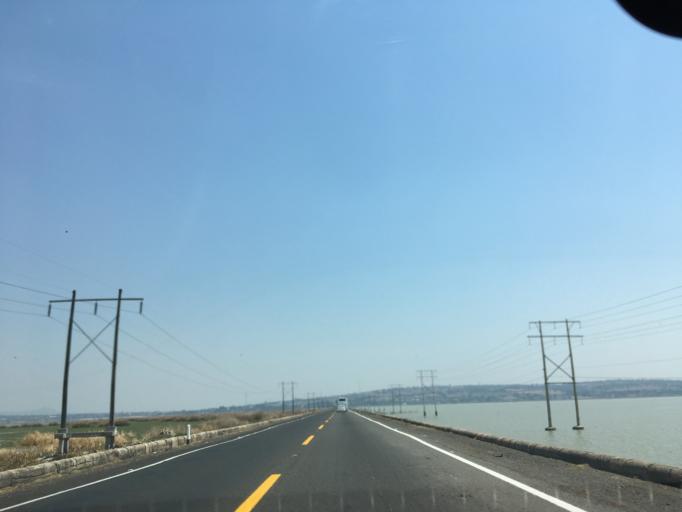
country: MX
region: Michoacan
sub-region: Cuitzeo
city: San Juan Benito Juarez (San Juan Tararameo)
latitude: 19.9366
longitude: -101.1387
